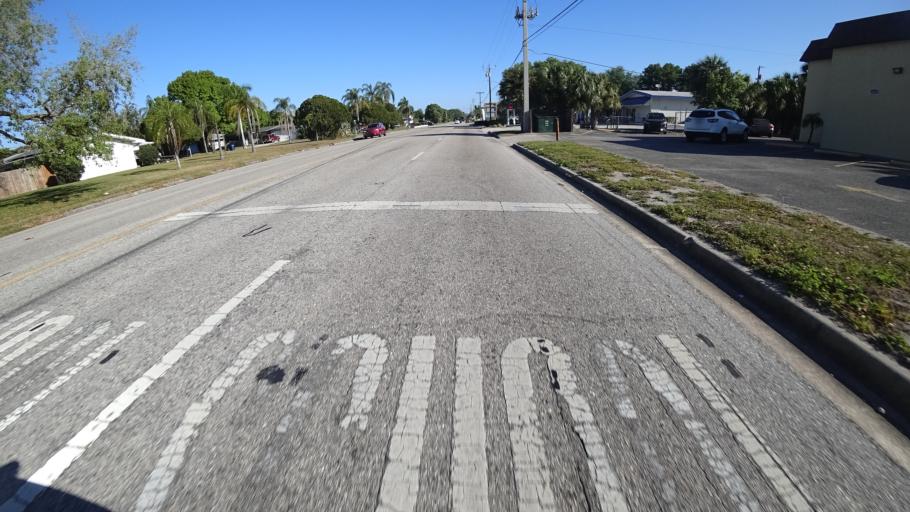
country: US
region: Florida
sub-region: Manatee County
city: South Bradenton
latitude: 27.4753
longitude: -82.5876
